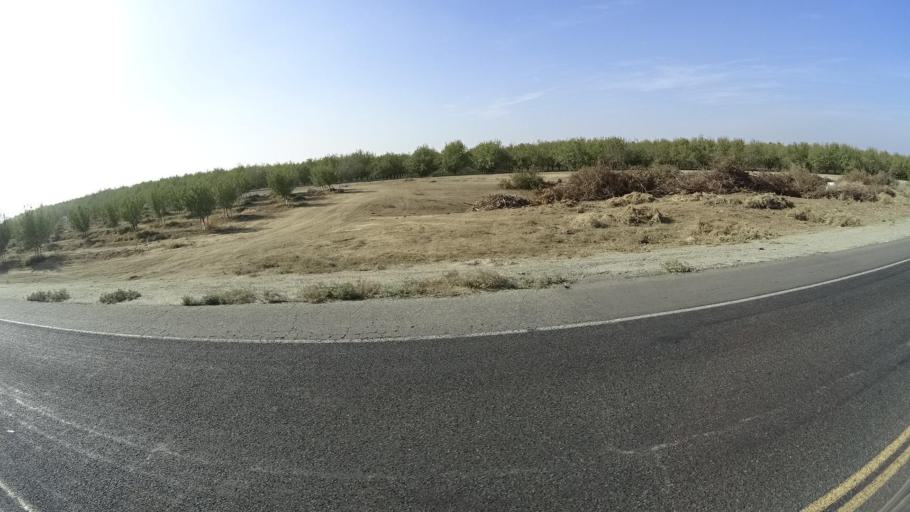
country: US
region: California
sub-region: Kern County
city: McFarland
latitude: 35.6573
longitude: -119.1957
